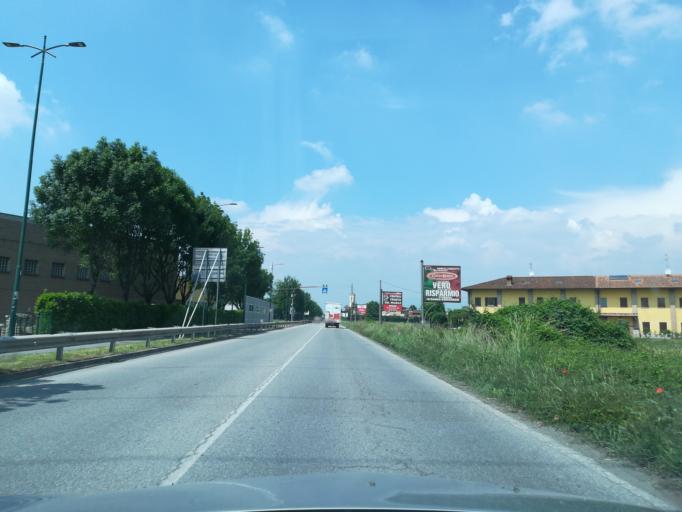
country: IT
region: Lombardy
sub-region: Provincia di Bergamo
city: Cavernago
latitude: 45.6259
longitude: 9.7693
